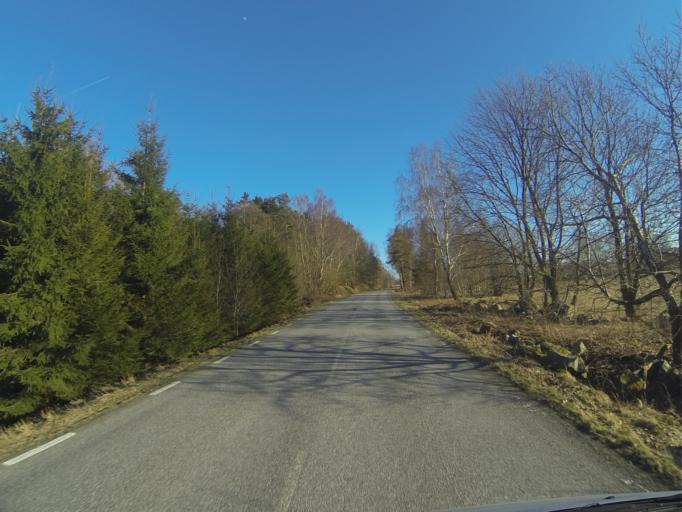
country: SE
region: Skane
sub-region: Horby Kommun
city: Hoerby
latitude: 55.9356
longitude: 13.6634
